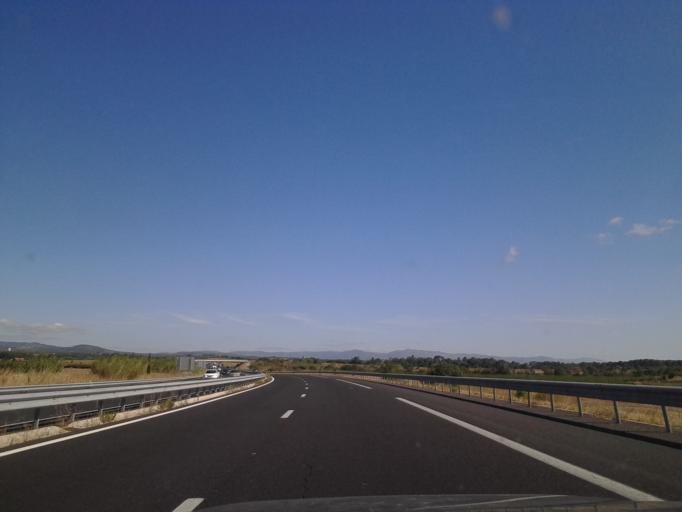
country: FR
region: Languedoc-Roussillon
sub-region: Departement de l'Herault
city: Lezignan-la-Cebe
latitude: 43.4947
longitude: 3.4465
